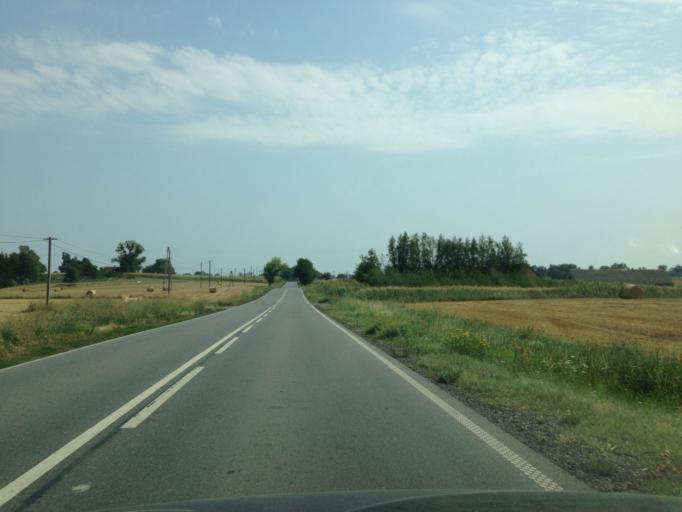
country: PL
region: Kujawsko-Pomorskie
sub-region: Powiat golubsko-dobrzynski
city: Radomin
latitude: 53.0989
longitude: 19.1426
